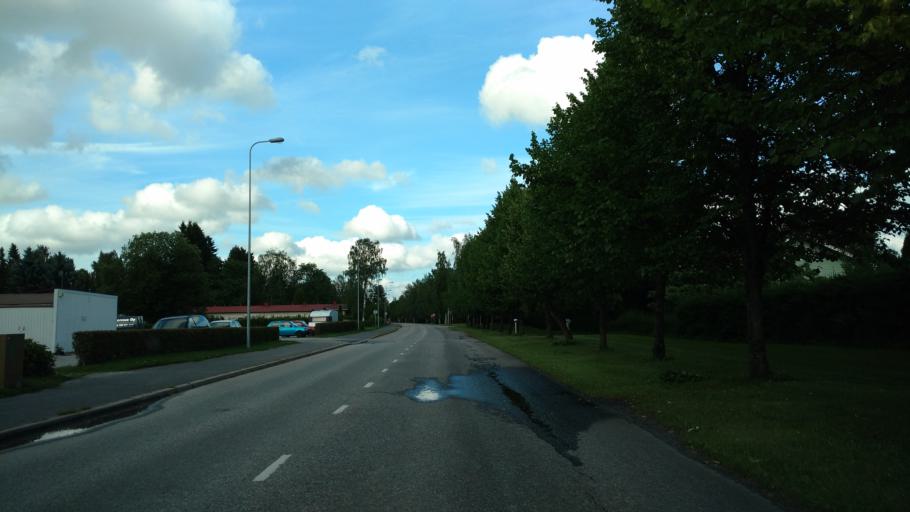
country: FI
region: Varsinais-Suomi
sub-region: Salo
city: Salo
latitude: 60.3972
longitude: 23.1413
